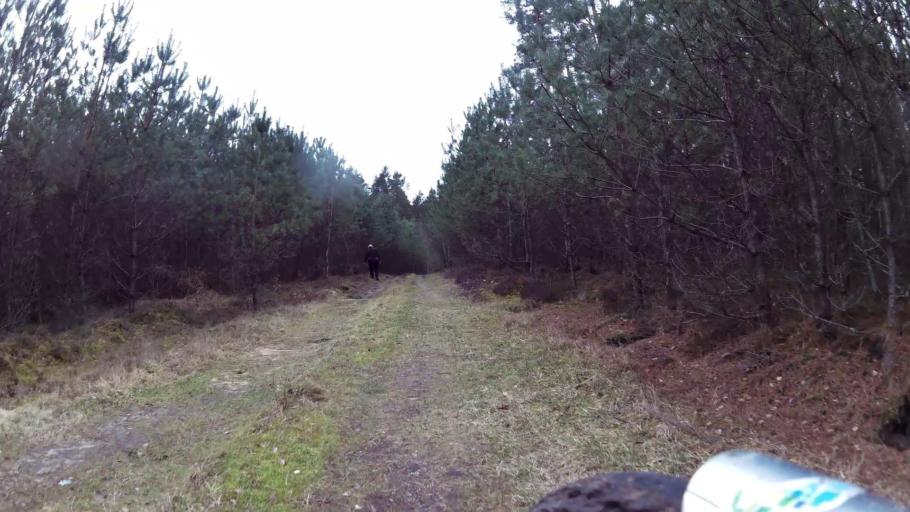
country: PL
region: Pomeranian Voivodeship
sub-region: Powiat bytowski
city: Kolczyglowy
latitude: 54.1538
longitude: 17.1820
